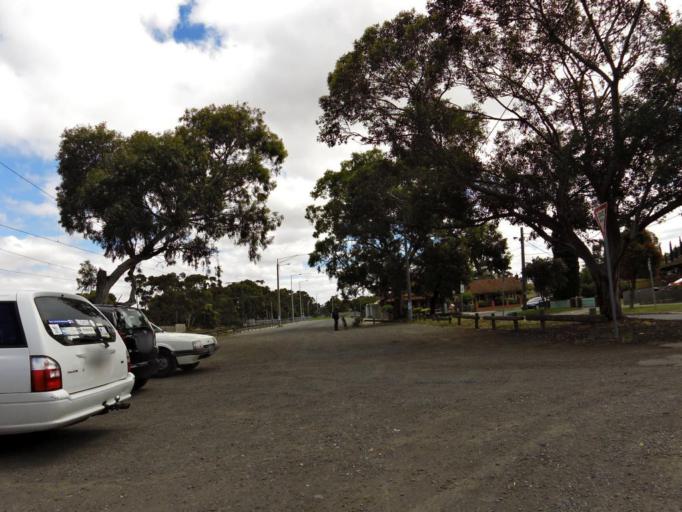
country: AU
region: Victoria
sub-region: Moreland
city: Fawkner
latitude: -37.7206
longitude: 144.9615
